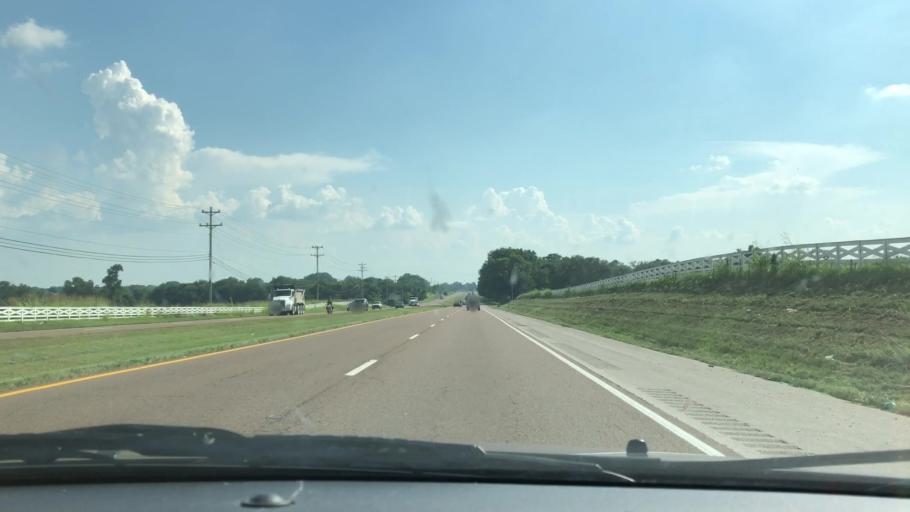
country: US
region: Tennessee
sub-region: Maury County
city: Spring Hill
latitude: 35.7295
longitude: -86.9586
